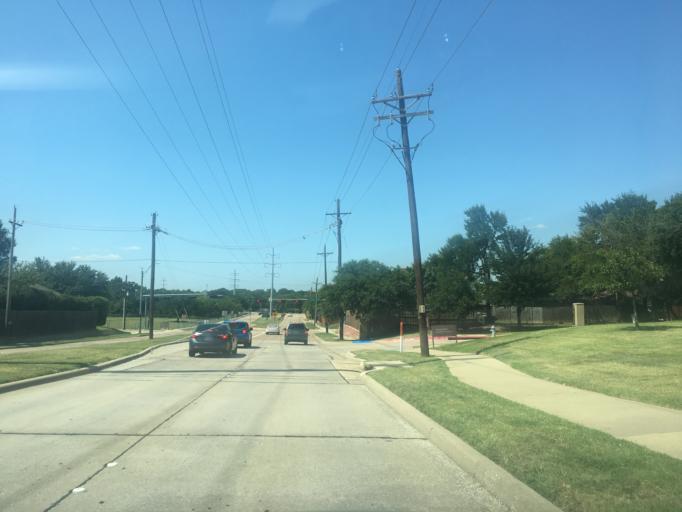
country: US
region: Texas
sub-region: Denton County
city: Lewisville
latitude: 33.0124
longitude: -97.0048
